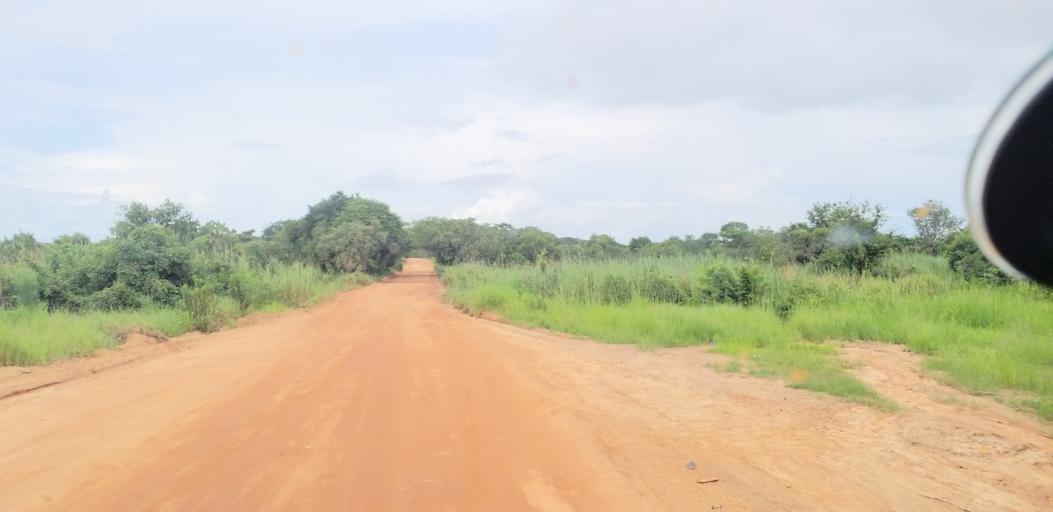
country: ZM
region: Lusaka
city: Lusaka
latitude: -15.1954
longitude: 28.4435
